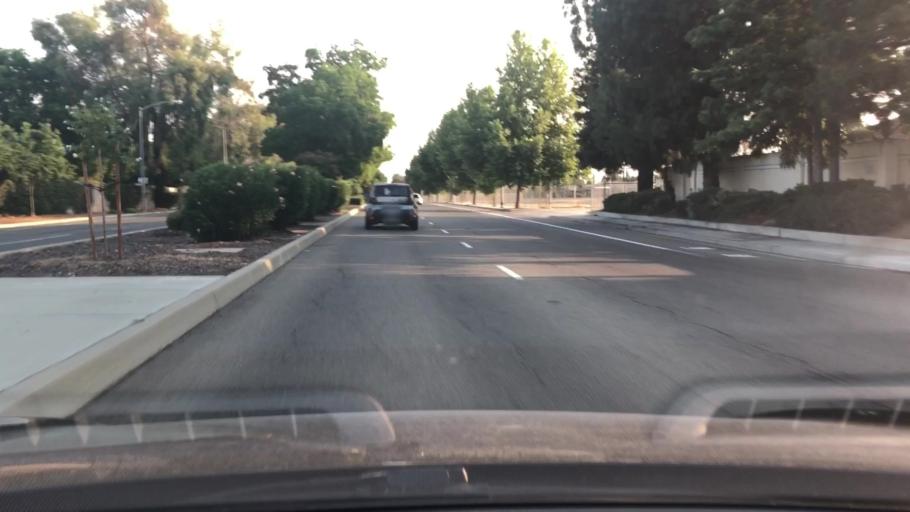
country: US
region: California
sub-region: Fresno County
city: Clovis
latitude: 36.8264
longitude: -119.7294
